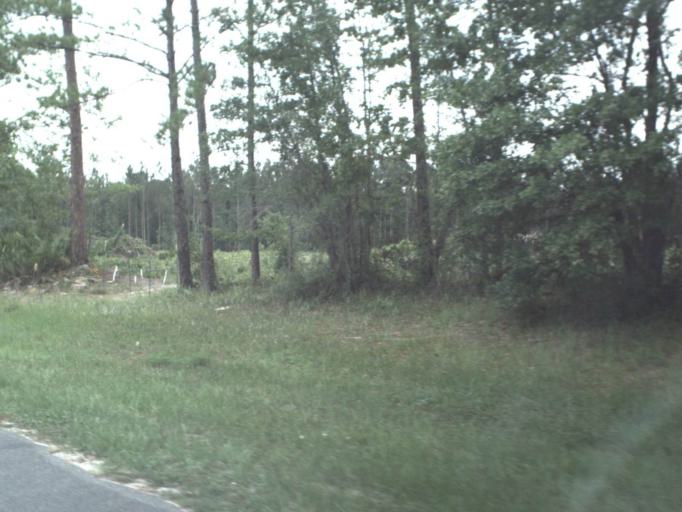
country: US
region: Florida
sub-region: Clay County
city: Middleburg
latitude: 29.9643
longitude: -81.8977
